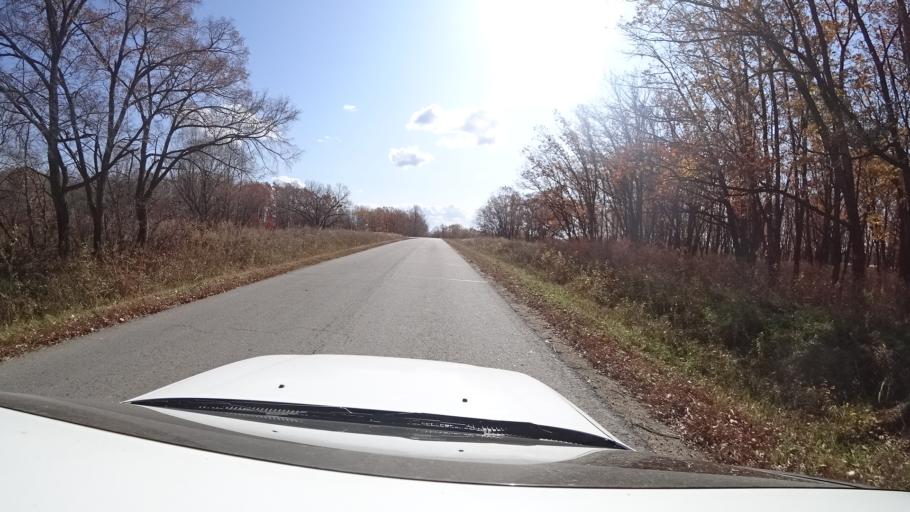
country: RU
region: Primorskiy
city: Lazo
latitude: 45.8692
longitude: 133.6612
